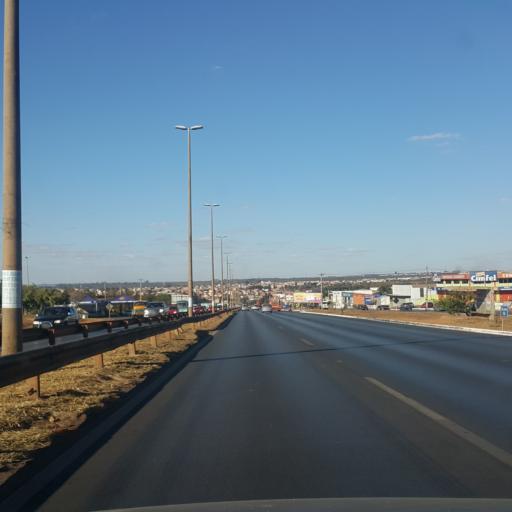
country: BR
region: Federal District
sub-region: Brasilia
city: Brasilia
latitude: -15.7890
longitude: -48.0174
